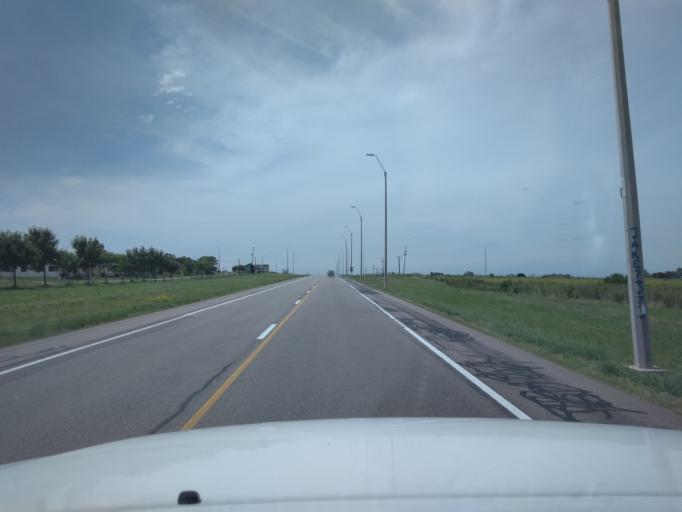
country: UY
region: Florida
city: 25 de Mayo
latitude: -34.2399
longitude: -56.2132
